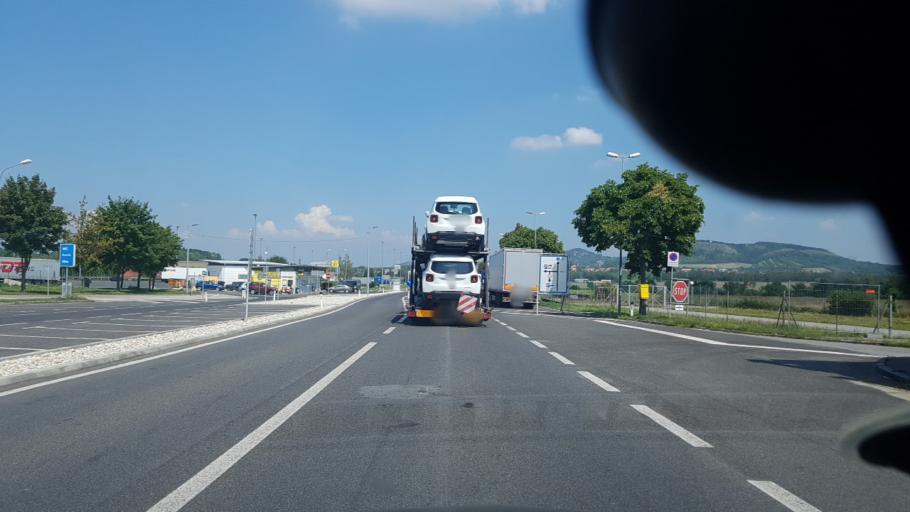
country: CZ
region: South Moravian
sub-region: Okres Breclav
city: Mikulov
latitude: 48.7790
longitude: 16.6405
